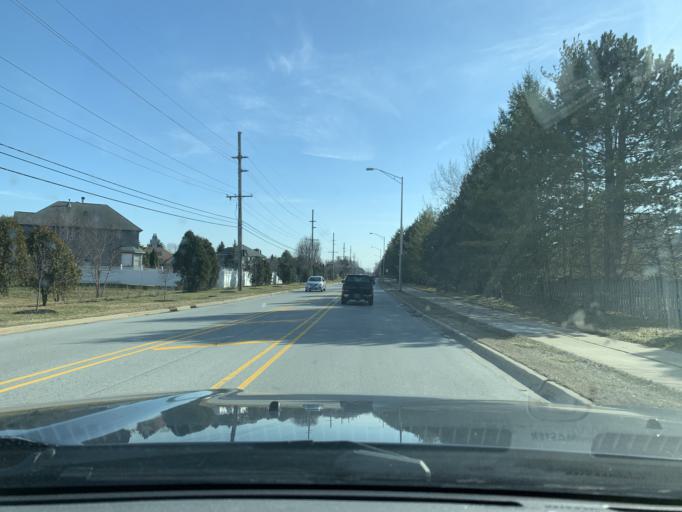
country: US
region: Indiana
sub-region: Lake County
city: Munster
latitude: 41.5304
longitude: -87.4904
